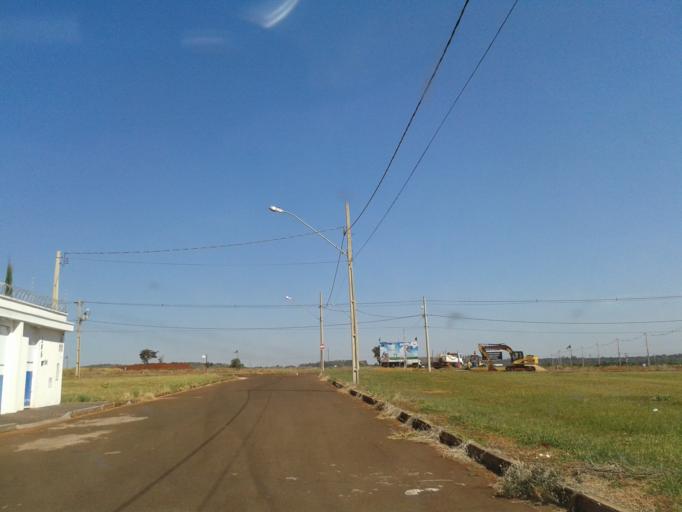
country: BR
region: Minas Gerais
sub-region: Ituiutaba
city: Ituiutaba
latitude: -19.0015
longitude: -49.4649
